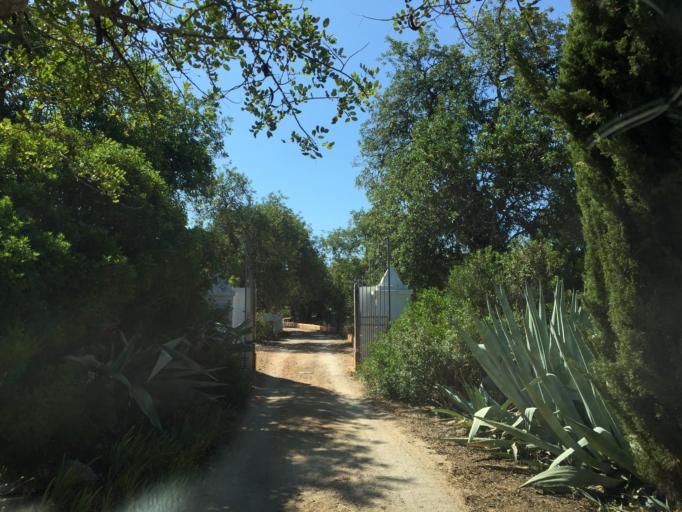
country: PT
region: Faro
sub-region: Loule
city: Vilamoura
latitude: 37.1178
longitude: -8.0824
